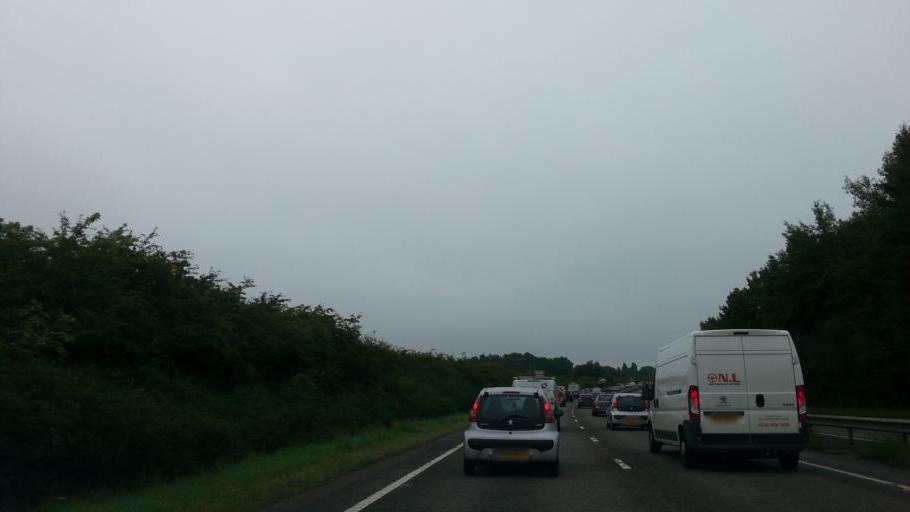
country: GB
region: England
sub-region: Warwickshire
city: Ryton on Dunsmore
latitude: 52.4026
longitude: -1.4320
